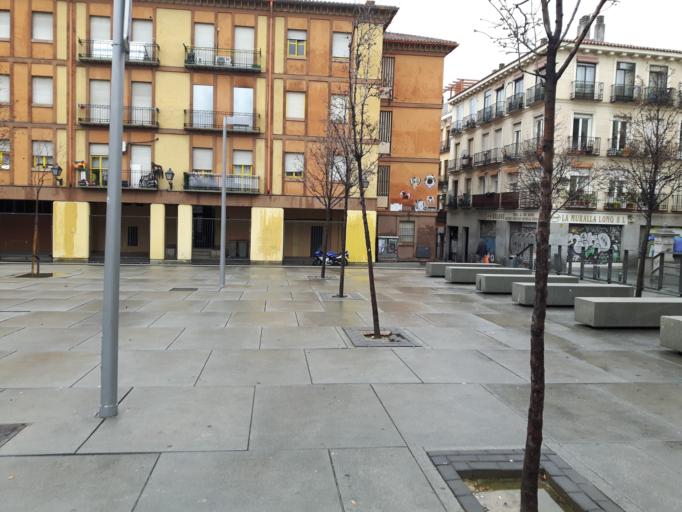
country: ES
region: Madrid
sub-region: Provincia de Madrid
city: Madrid
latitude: 40.4097
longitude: -3.7039
